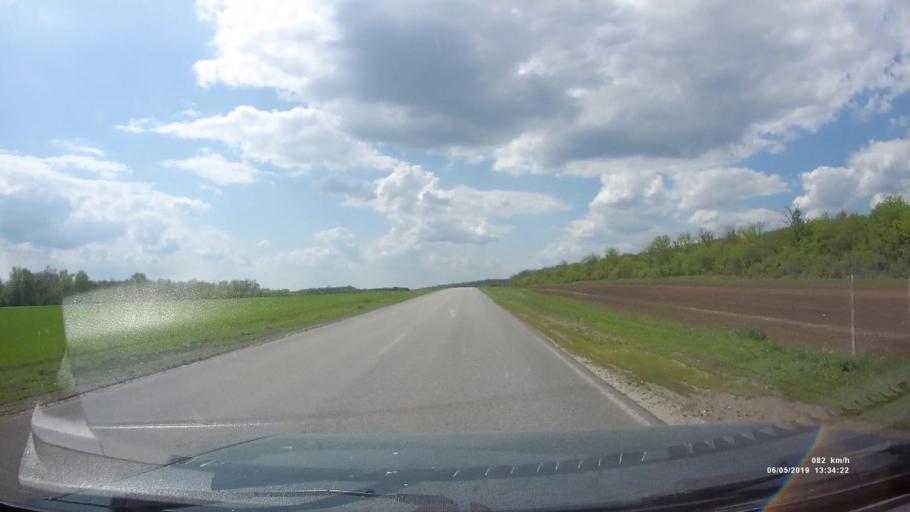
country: RU
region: Rostov
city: Ust'-Donetskiy
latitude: 47.6927
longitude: 40.7640
